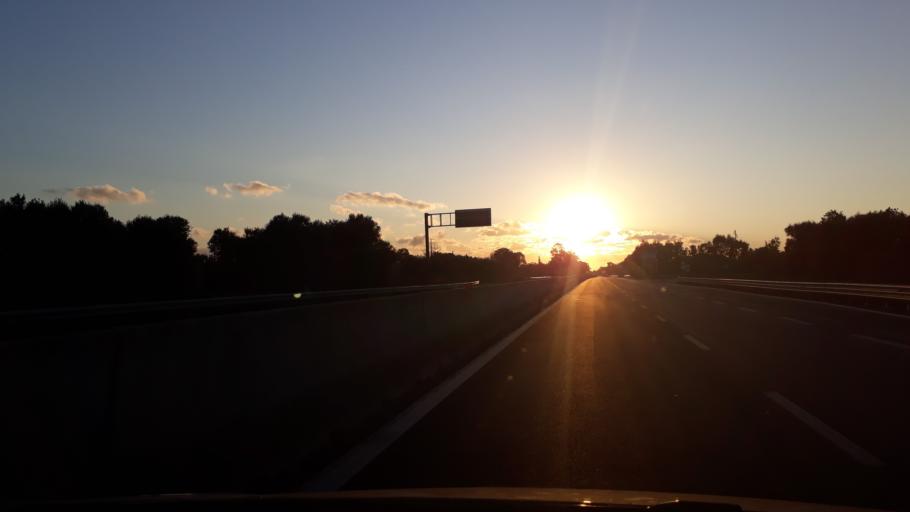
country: IT
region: Apulia
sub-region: Provincia di Brindisi
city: Montalbano
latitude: 40.8006
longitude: 17.5393
